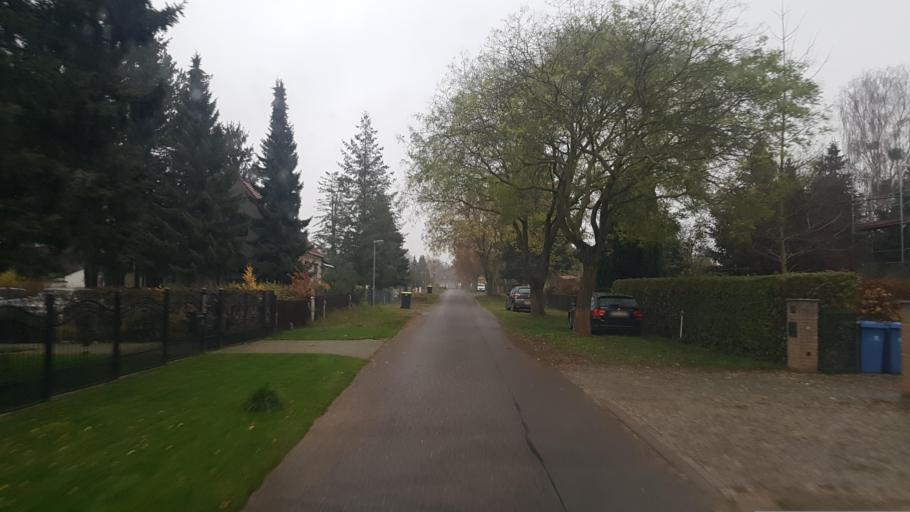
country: DE
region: Brandenburg
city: Michendorf
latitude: 52.3066
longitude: 13.0187
